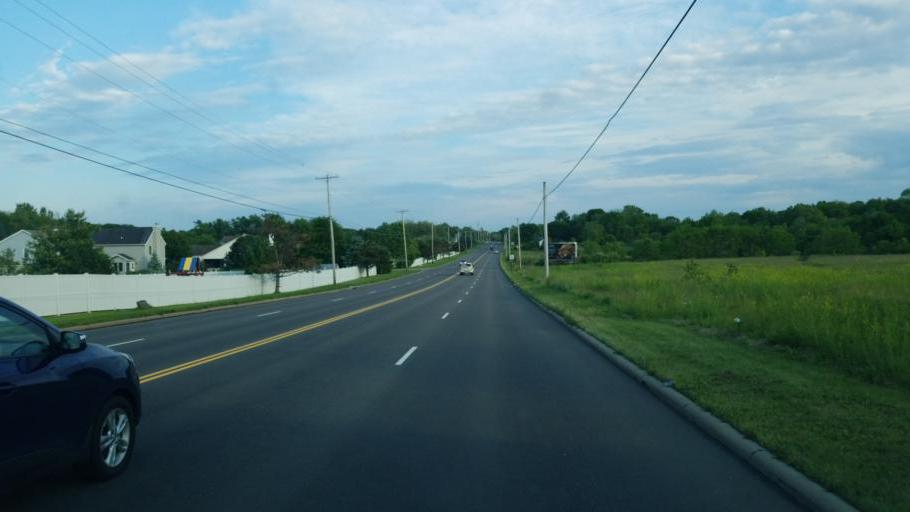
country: US
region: Ohio
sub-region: Stark County
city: Greentown
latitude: 40.9451
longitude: -81.4045
